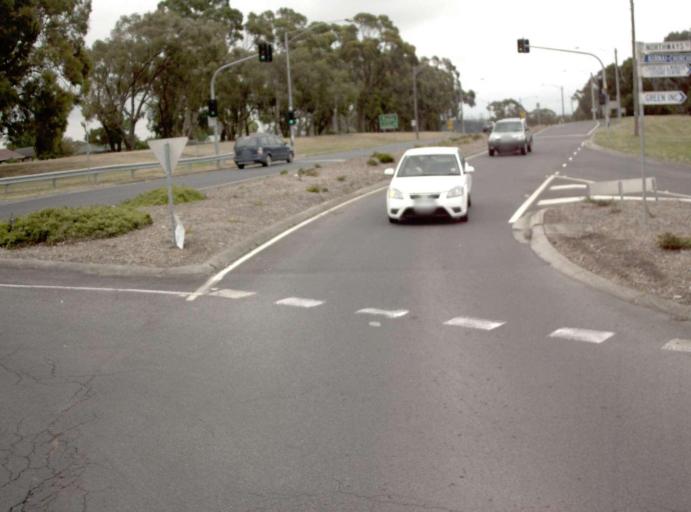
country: AU
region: Victoria
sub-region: Latrobe
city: Morwell
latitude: -38.3084
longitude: 146.4208
